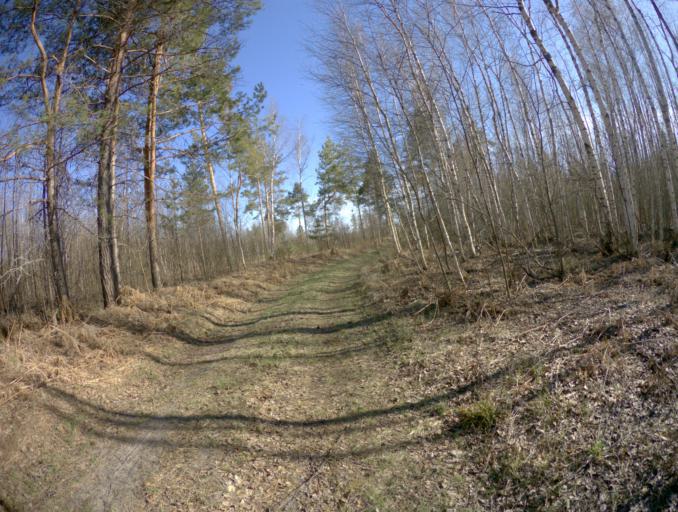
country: RU
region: Vladimir
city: Ivanishchi
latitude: 55.7124
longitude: 40.4345
